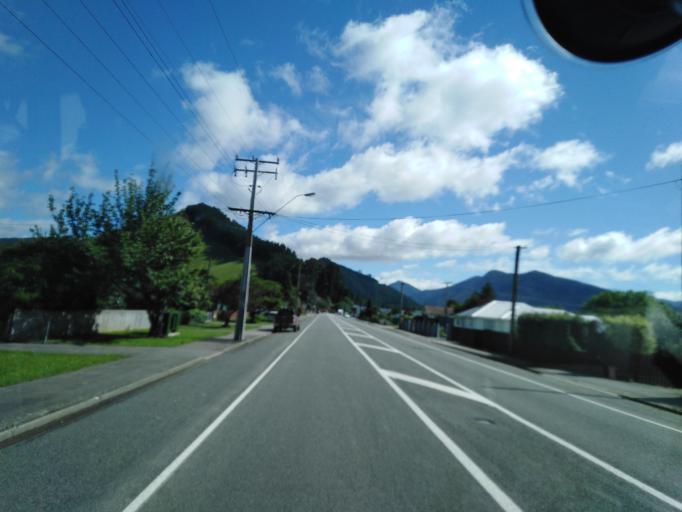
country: NZ
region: Nelson
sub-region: Nelson City
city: Nelson
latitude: -41.2302
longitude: 173.5822
